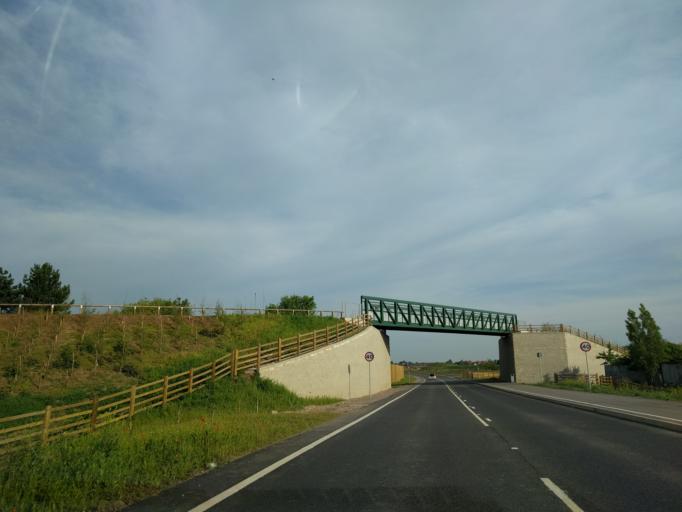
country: GB
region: England
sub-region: Nottinghamshire
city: Newark on Trent
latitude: 53.0502
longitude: -0.7996
